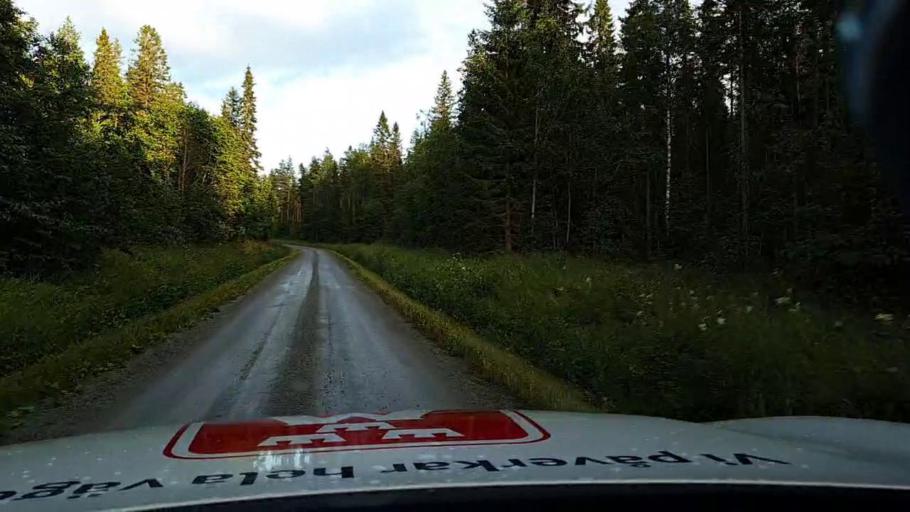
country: SE
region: Jaemtland
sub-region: Bergs Kommun
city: Hoverberg
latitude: 62.8516
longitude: 14.5398
